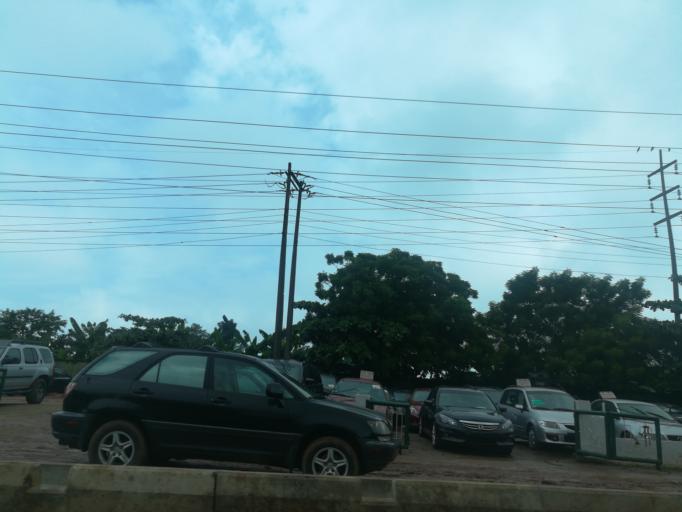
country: NG
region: Lagos
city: Ikorodu
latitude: 6.6562
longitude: 3.5194
